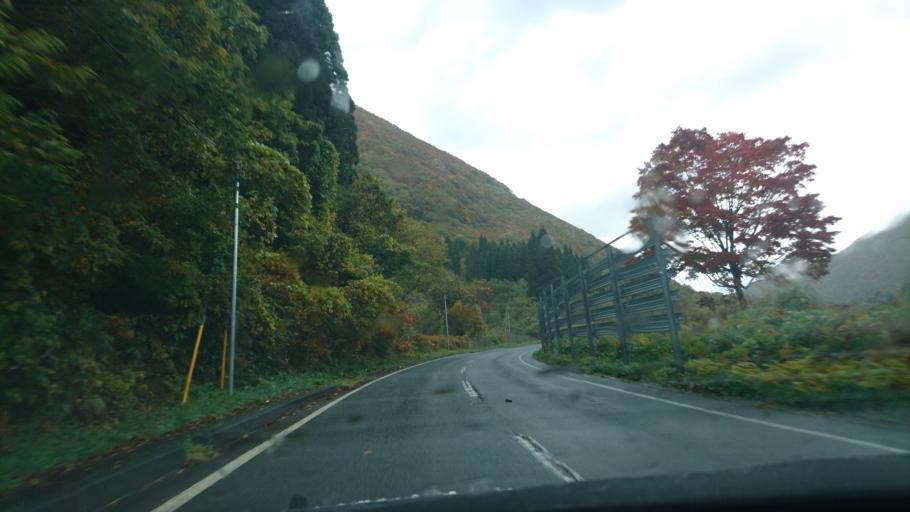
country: JP
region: Iwate
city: Shizukuishi
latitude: 39.6068
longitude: 140.9315
